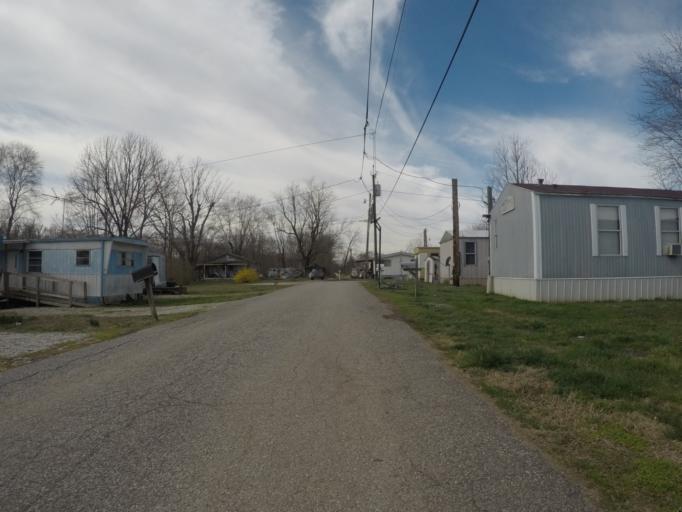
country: US
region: West Virginia
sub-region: Cabell County
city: Pea Ridge
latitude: 38.4156
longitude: -82.3537
